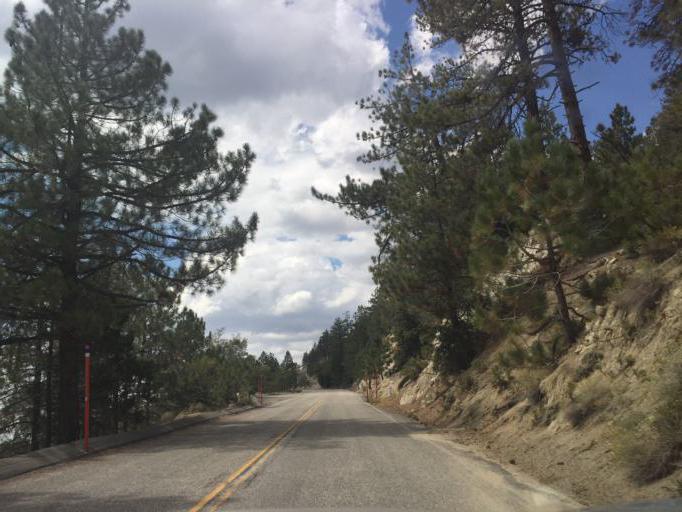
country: US
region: California
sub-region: Los Angeles County
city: Littlerock
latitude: 34.3513
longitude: -117.9423
